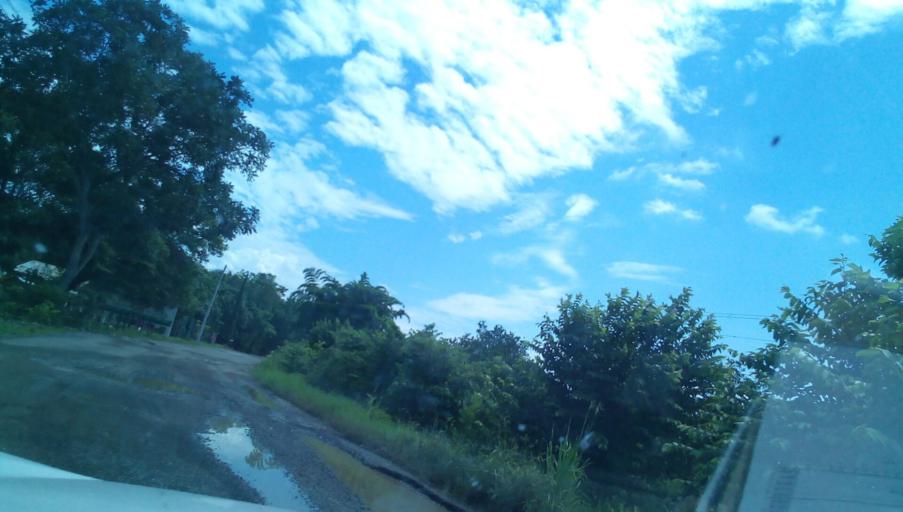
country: MX
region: Veracruz
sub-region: Alamo Temapache
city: Vegas de la Soledad y Soledad Dos
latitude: 20.9070
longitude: -97.9289
